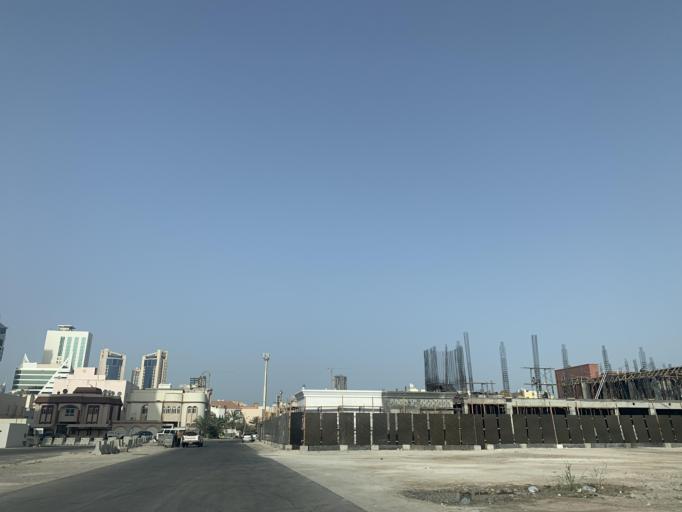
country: BH
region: Manama
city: Jidd Hafs
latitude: 26.2281
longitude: 50.5459
